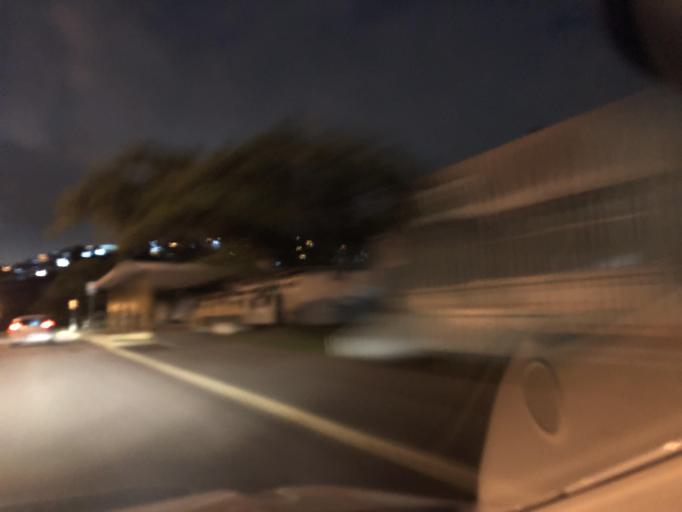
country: BR
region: Santa Catarina
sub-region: Florianopolis
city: Carvoeira
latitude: -27.6017
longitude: -48.5221
